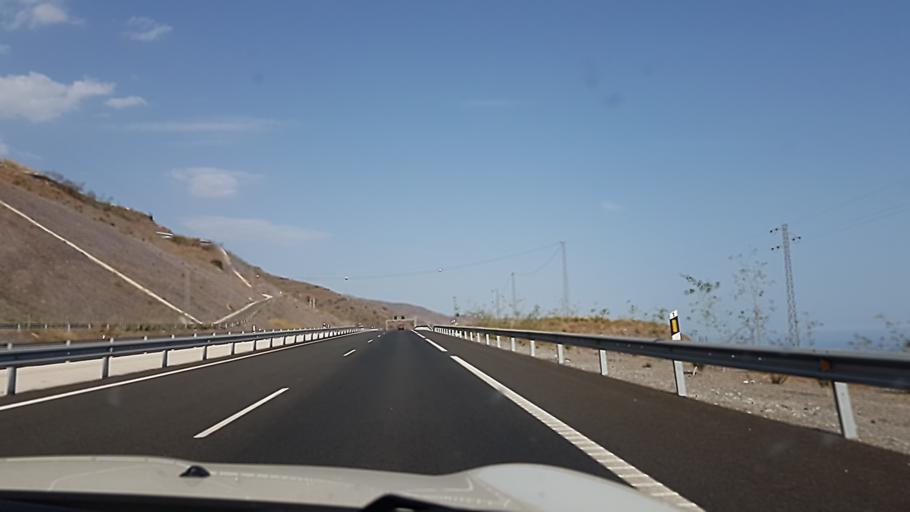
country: ES
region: Andalusia
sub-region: Provincia de Granada
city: Sorvilan
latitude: 36.7541
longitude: -3.2677
